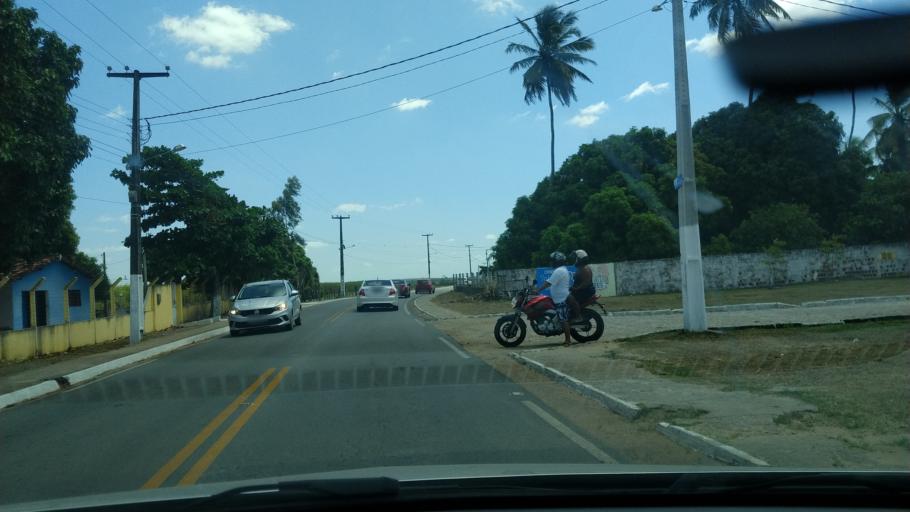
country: BR
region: Rio Grande do Norte
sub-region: Goianinha
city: Goianinha
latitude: -6.2431
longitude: -35.1799
